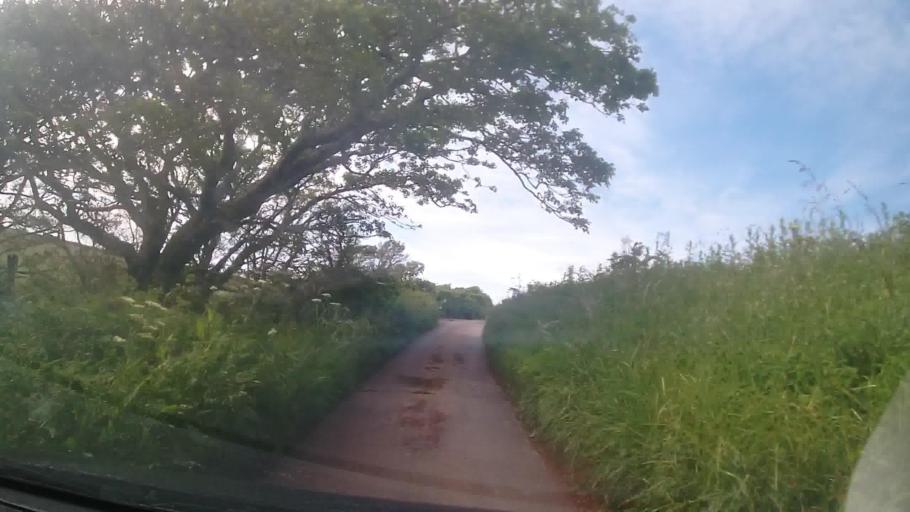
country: GB
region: England
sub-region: Devon
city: Salcombe
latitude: 50.2263
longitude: -3.6580
